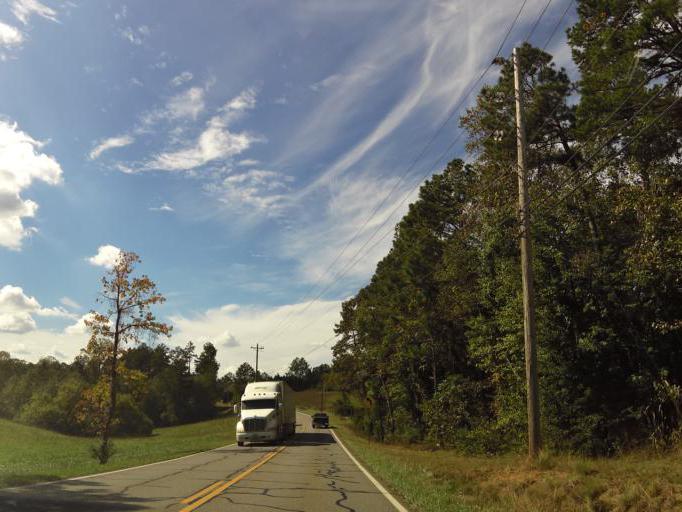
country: US
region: Georgia
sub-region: Pickens County
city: Nelson
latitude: 34.4178
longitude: -84.3093
